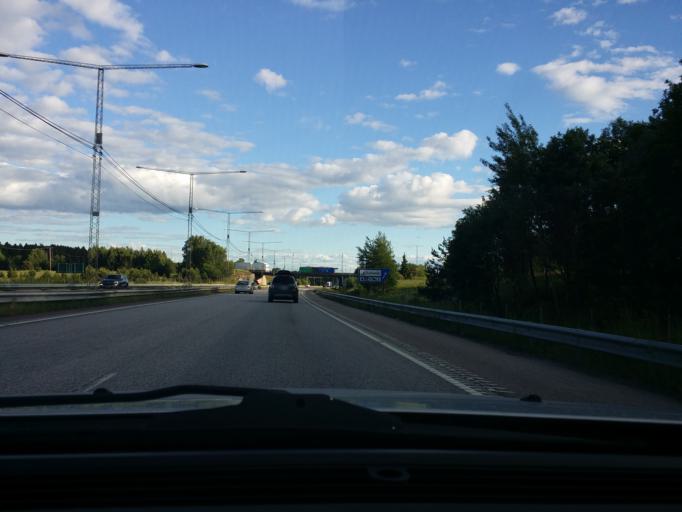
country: SE
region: Stockholm
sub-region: Sigtuna Kommun
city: Rosersberg
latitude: 59.6063
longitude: 17.8995
